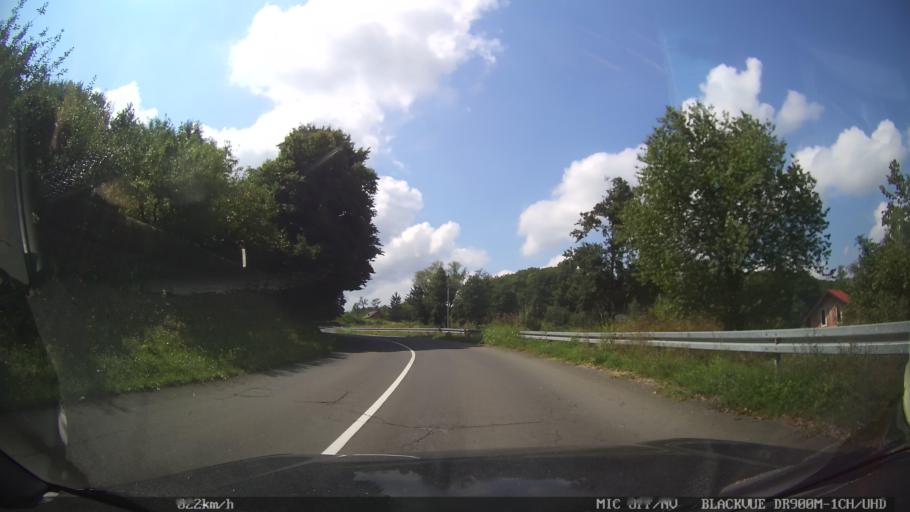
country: HR
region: Sisacko-Moslavacka
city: Gvozd
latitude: 45.5253
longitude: 15.8764
